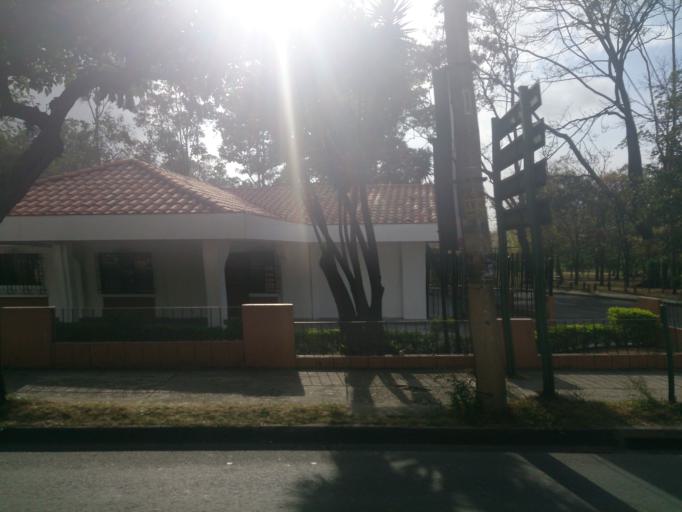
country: CR
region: San Jose
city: San Jose
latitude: 9.9366
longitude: -84.0983
